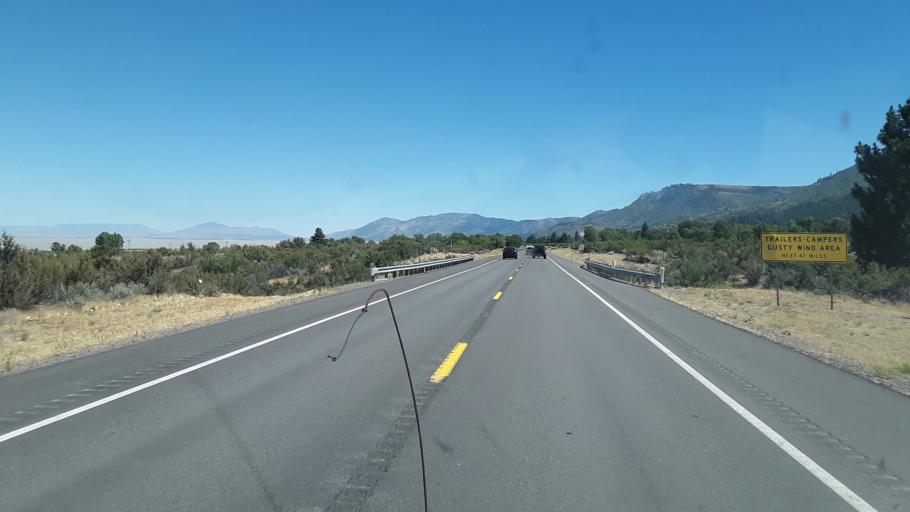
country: US
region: California
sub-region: Lassen County
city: Janesville
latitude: 40.2792
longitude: -120.4863
